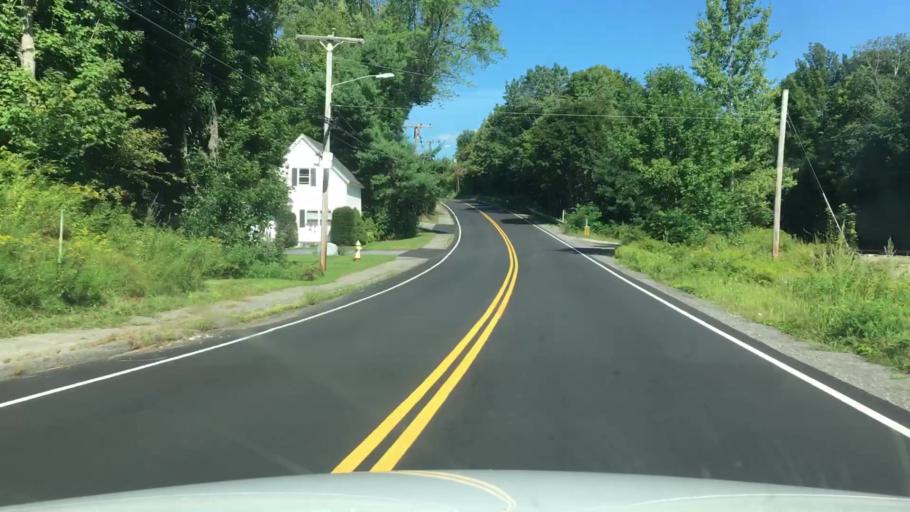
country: US
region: Maine
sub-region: Kennebec County
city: Randolph
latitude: 44.2239
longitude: -69.7656
